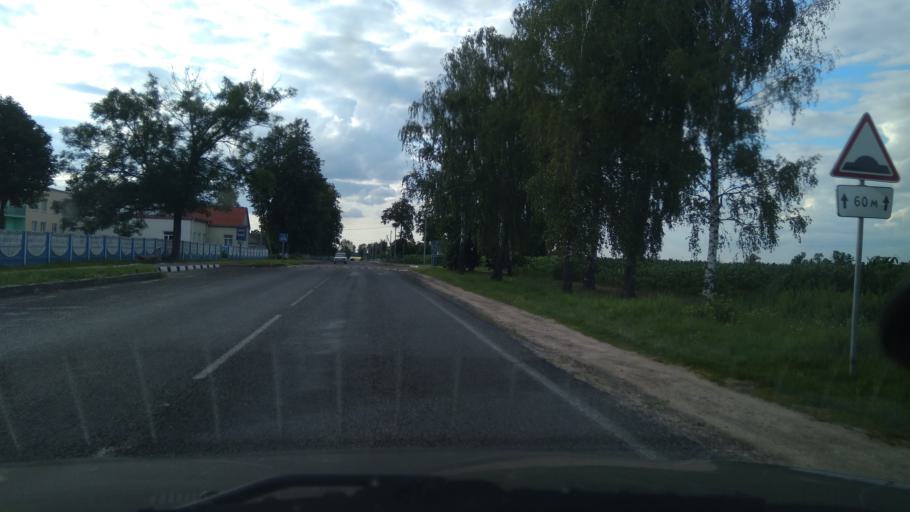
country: BY
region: Grodnenskaya
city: Masty
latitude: 53.3197
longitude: 24.6872
